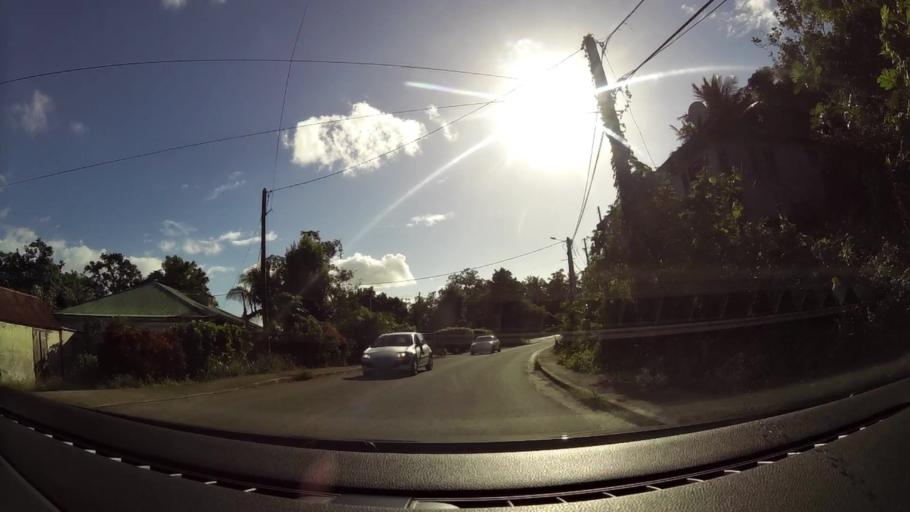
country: GP
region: Guadeloupe
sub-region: Guadeloupe
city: Petit-Canal
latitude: 16.3240
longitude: -61.4423
